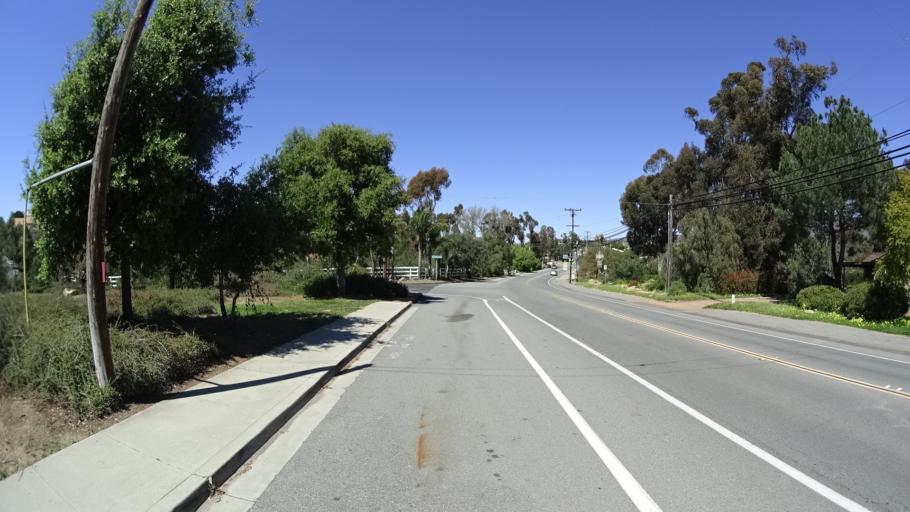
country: US
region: California
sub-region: San Diego County
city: Alpine
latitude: 32.8212
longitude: -116.7764
